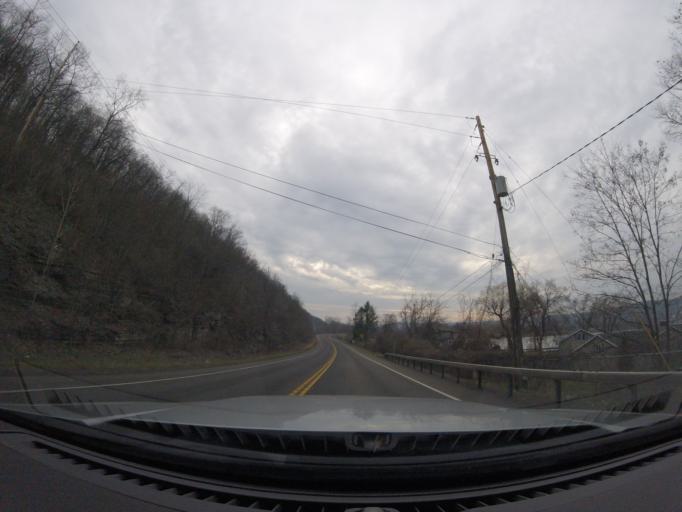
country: US
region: New York
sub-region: Schuyler County
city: Watkins Glen
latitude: 42.3905
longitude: -76.8557
